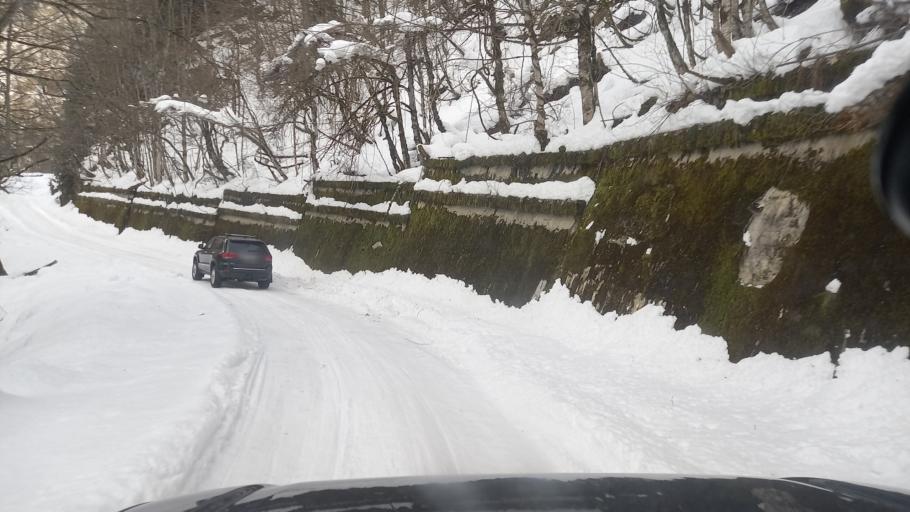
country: GE
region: Abkhazia
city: Gagra
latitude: 43.4788
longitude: 40.5482
